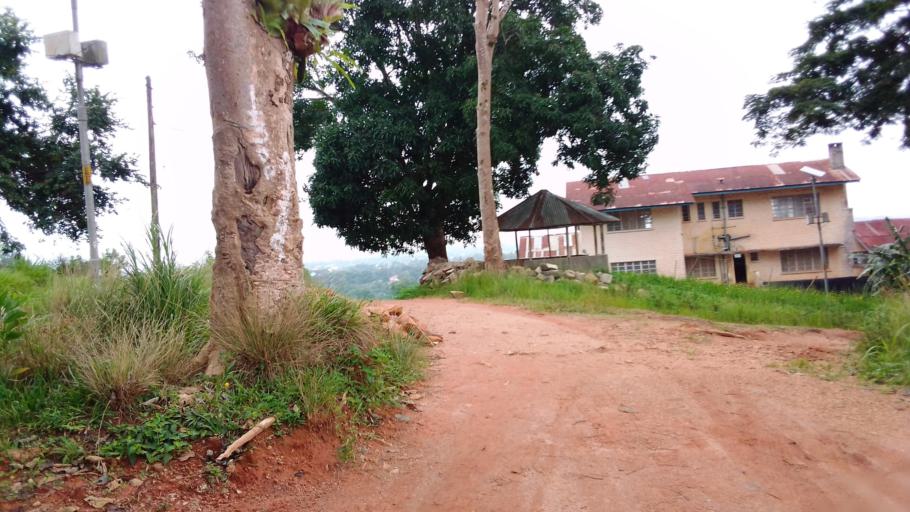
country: SL
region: Eastern Province
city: Kenema
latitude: 7.8939
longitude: -11.1905
